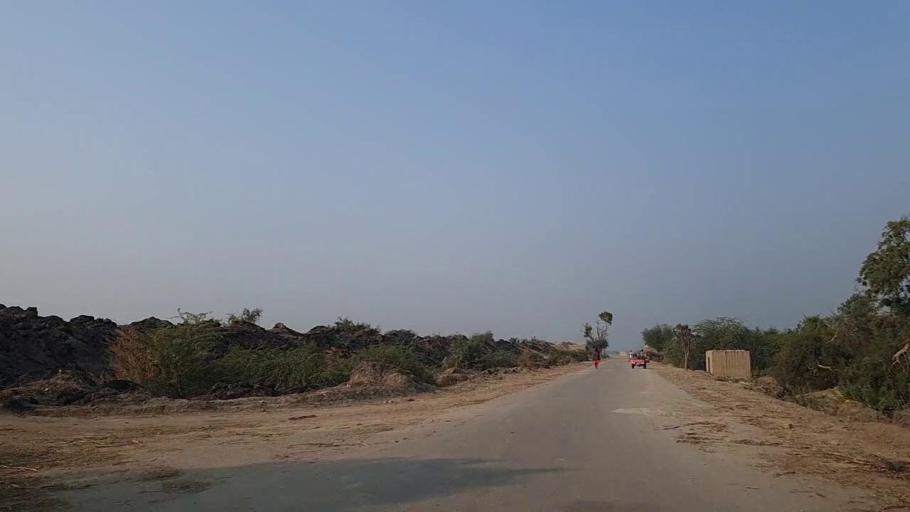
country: PK
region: Sindh
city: Sann
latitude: 26.1108
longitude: 68.1501
